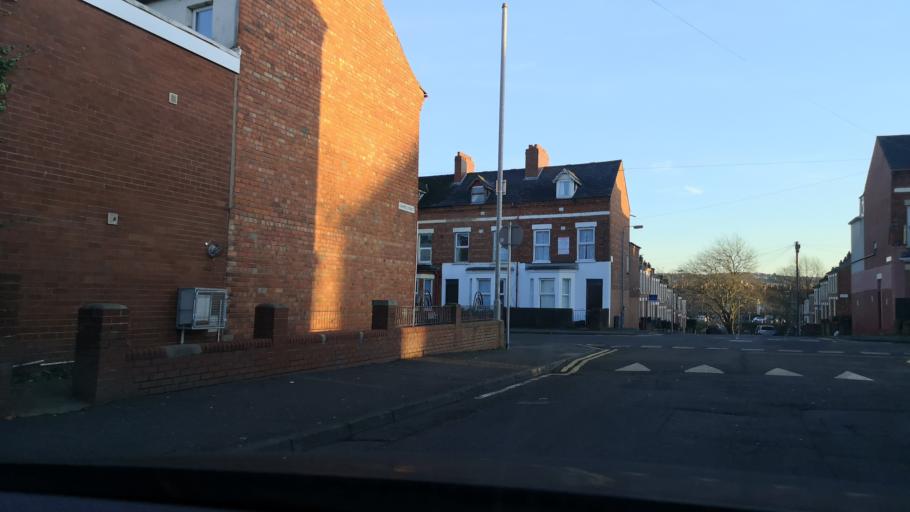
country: GB
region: Northern Ireland
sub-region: City of Belfast
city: Belfast
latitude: 54.5830
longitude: -5.9272
